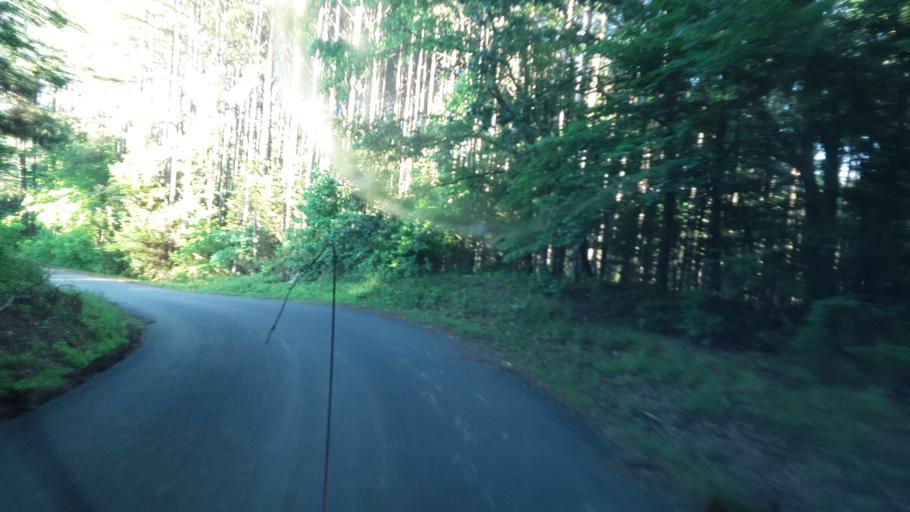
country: US
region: Virginia
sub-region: Pittsylvania County
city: Chatham
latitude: 36.8513
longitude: -79.4522
